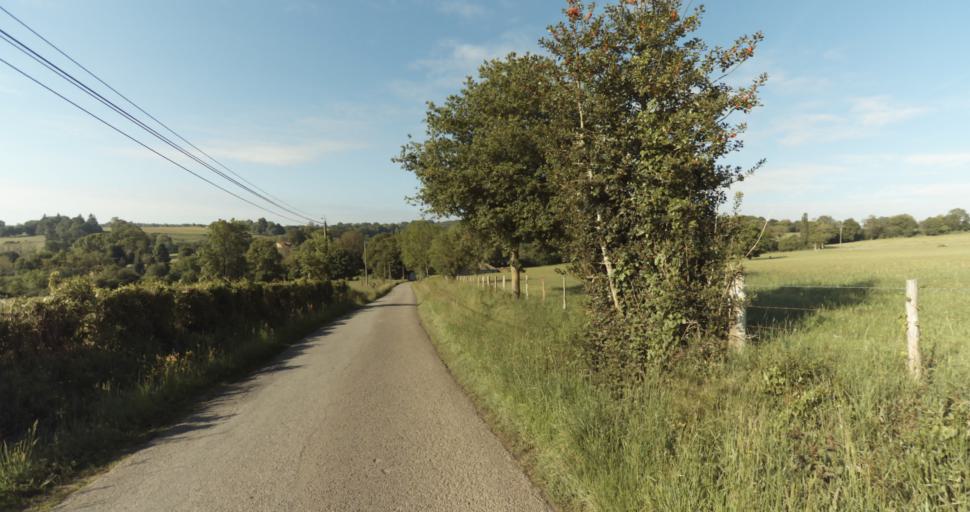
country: FR
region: Limousin
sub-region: Departement de la Haute-Vienne
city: Solignac
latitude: 45.7418
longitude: 1.2725
